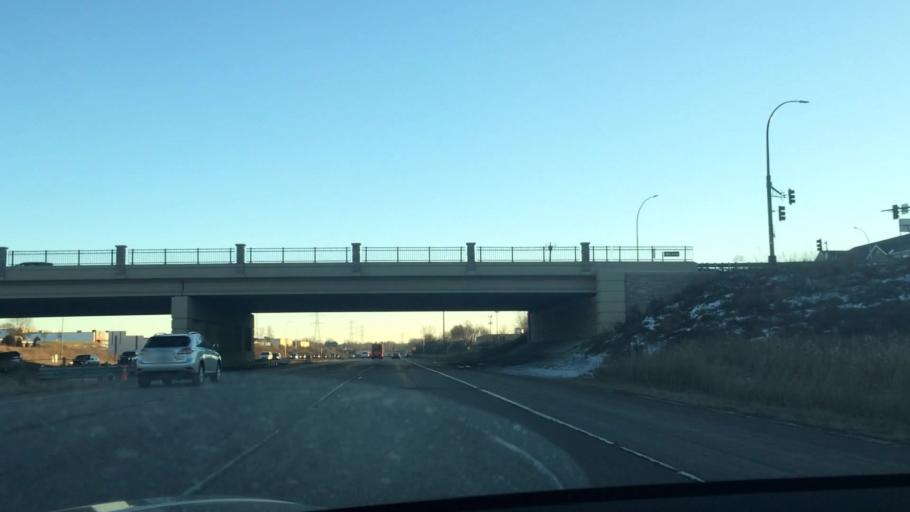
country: US
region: Minnesota
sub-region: Ramsey County
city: New Brighton
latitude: 45.0799
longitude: -93.1865
